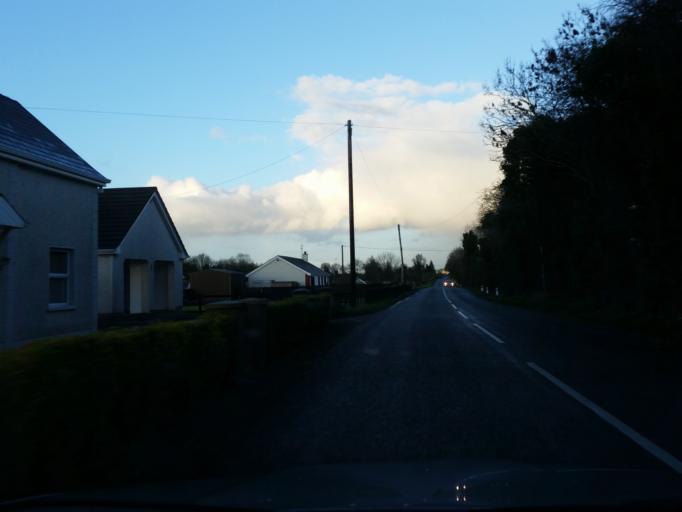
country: GB
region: Northern Ireland
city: Lisnaskea
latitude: 54.2186
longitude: -7.4638
